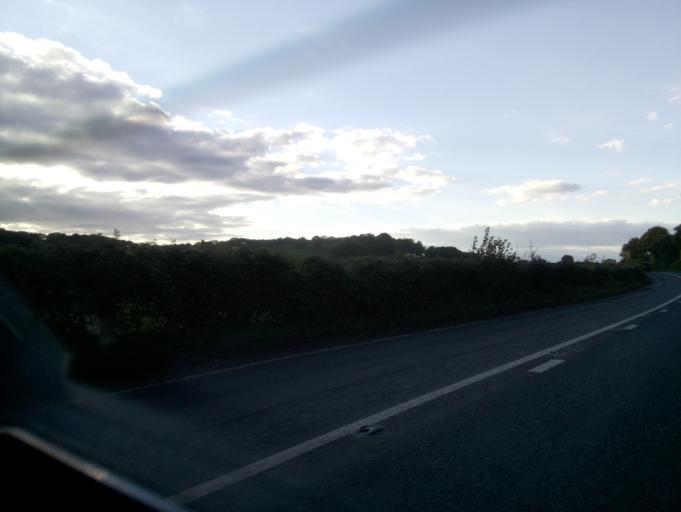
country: GB
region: England
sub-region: Herefordshire
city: Ledbury
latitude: 52.0468
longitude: -2.4414
